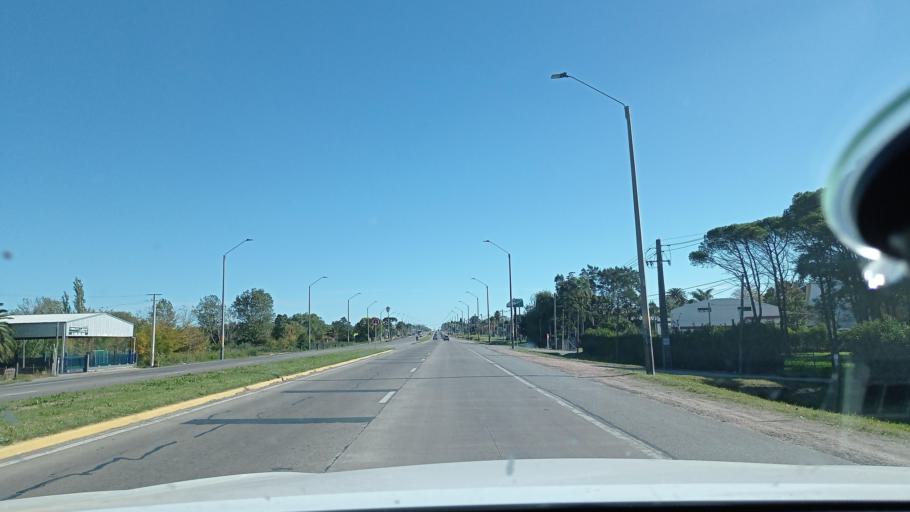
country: UY
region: Canelones
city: Joaquin Suarez
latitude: -34.7558
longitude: -56.0063
